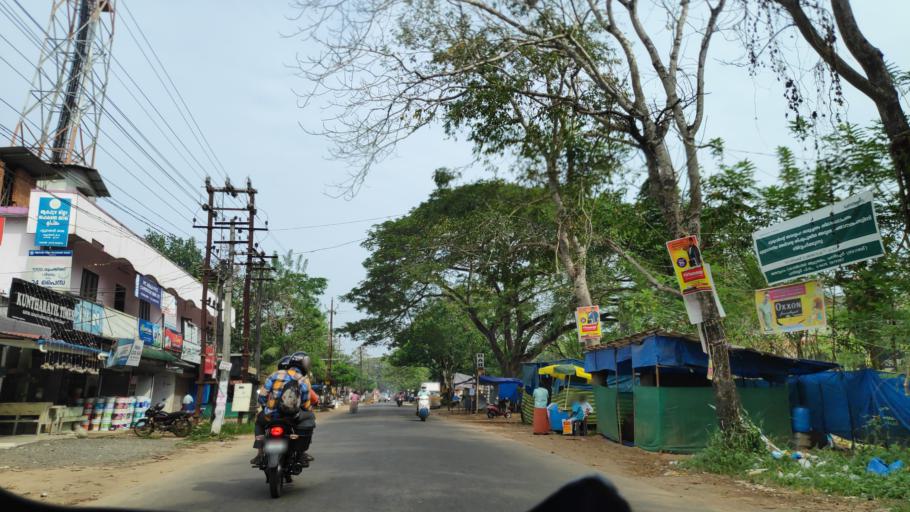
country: IN
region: Kerala
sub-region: Alappuzha
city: Kutiatodu
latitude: 9.7981
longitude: 76.3540
